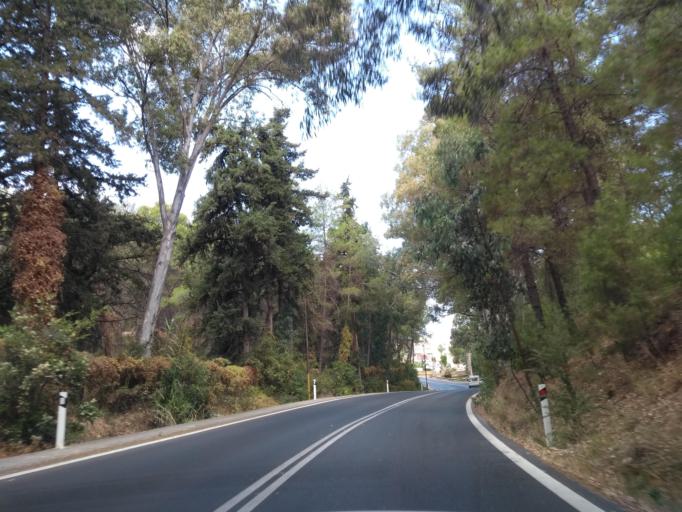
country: GR
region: Crete
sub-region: Nomos Chanias
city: Souda
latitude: 35.4847
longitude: 24.0867
